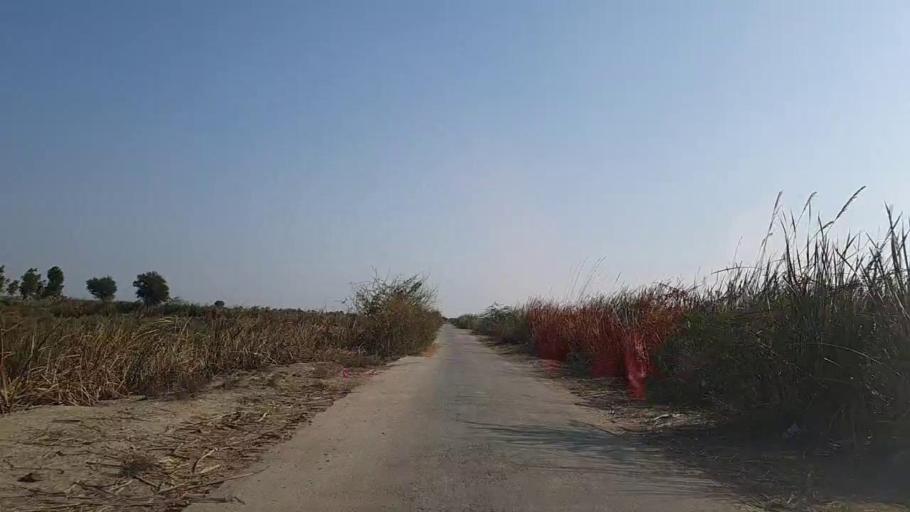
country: PK
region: Sindh
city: Sanghar
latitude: 25.9391
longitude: 69.0558
